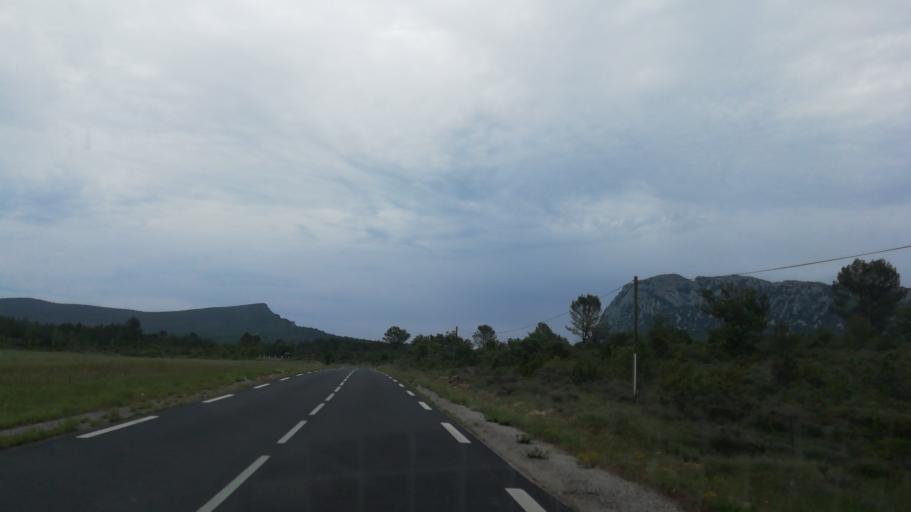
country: FR
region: Languedoc-Roussillon
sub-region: Departement de l'Herault
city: Saint-Martin-de-Londres
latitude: 43.7948
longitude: 3.7789
